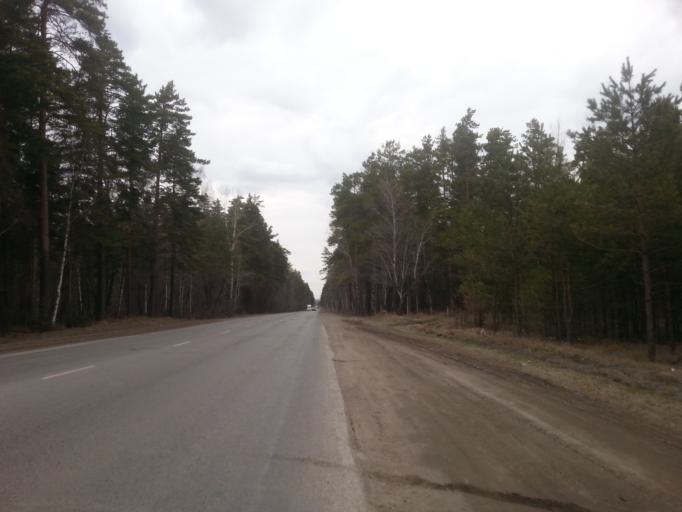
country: RU
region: Altai Krai
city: Yuzhnyy
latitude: 53.2745
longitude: 83.7216
